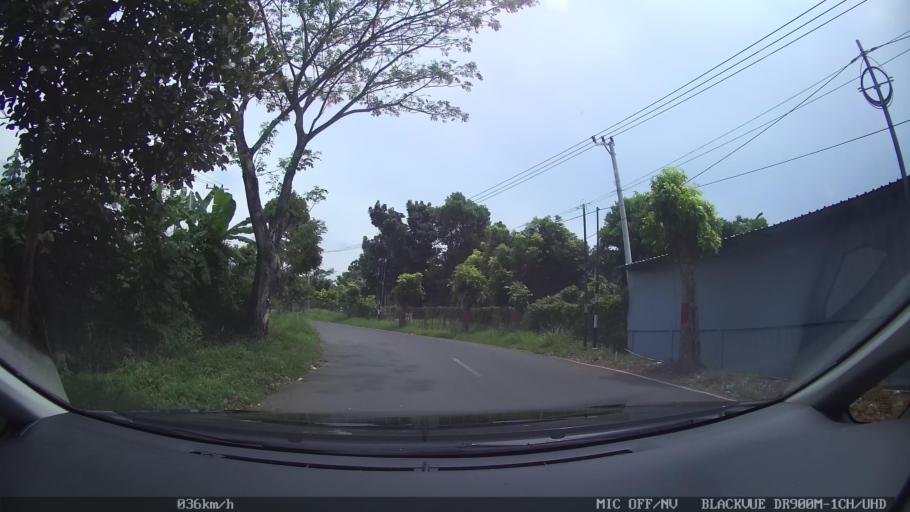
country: ID
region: Lampung
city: Bandarlampung
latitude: -5.4344
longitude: 105.2474
